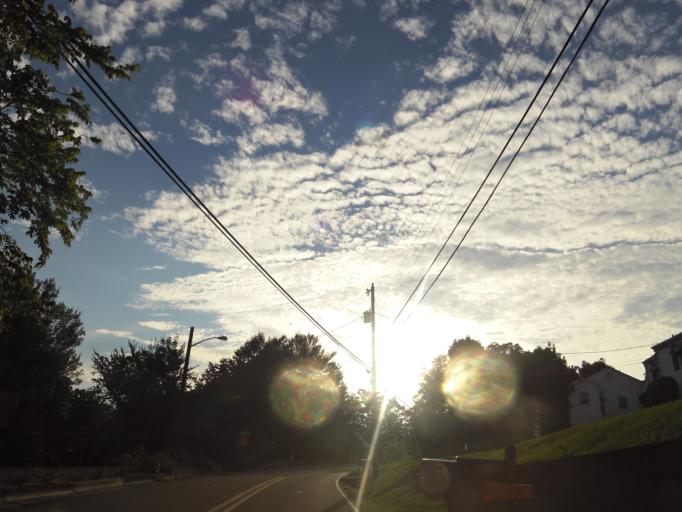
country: US
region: Tennessee
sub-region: Knox County
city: Knoxville
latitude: 36.0412
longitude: -83.9374
